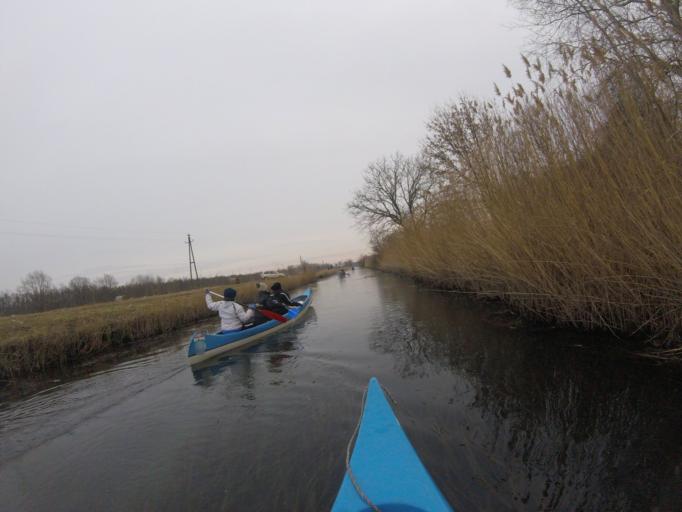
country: HU
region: Zala
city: Heviz
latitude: 46.7795
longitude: 17.1982
